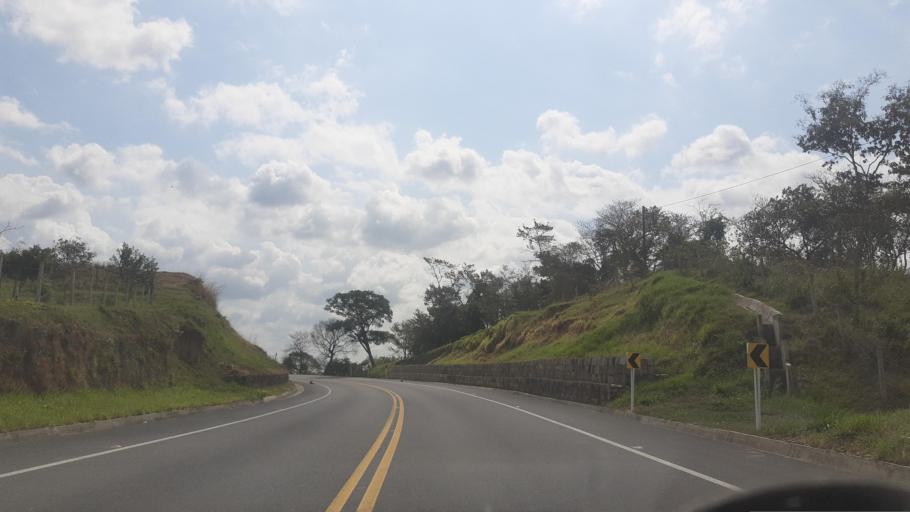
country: CO
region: Casanare
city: Monterrey
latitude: 4.8302
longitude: -72.8176
